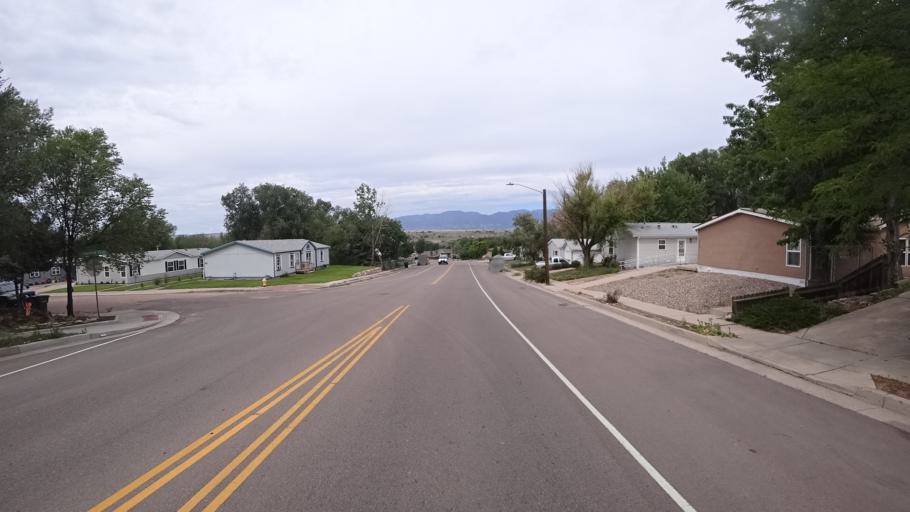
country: US
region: Colorado
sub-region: El Paso County
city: Fountain
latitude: 38.6972
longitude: -104.7019
